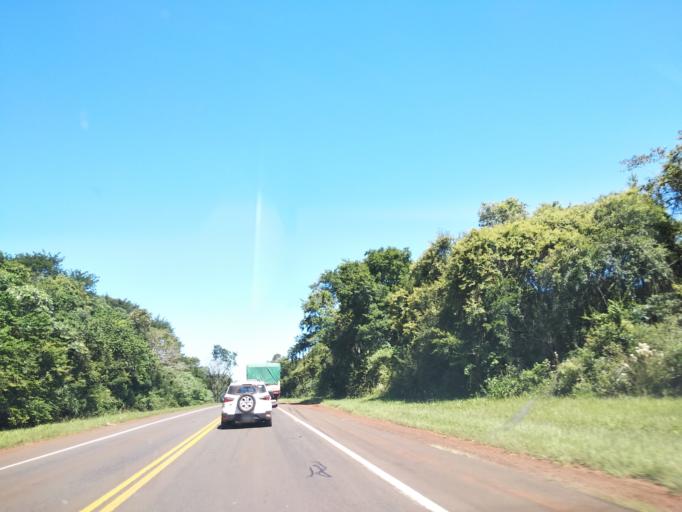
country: AR
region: Misiones
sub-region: Departamento de Iguazu
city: Puerto Iguazu
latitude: -25.6956
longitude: -54.5149
